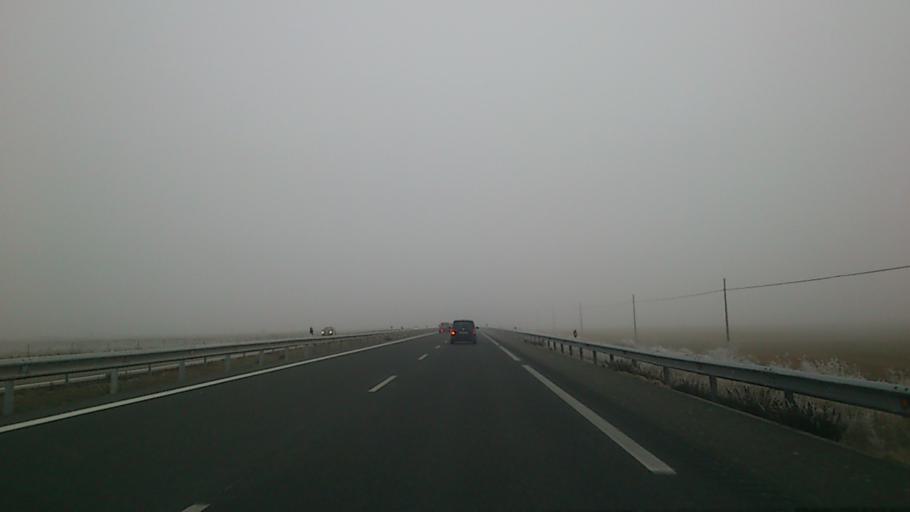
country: ES
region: Castille-La Mancha
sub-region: Provincia de Guadalajara
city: Almadrones
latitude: 40.8807
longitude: -2.7905
